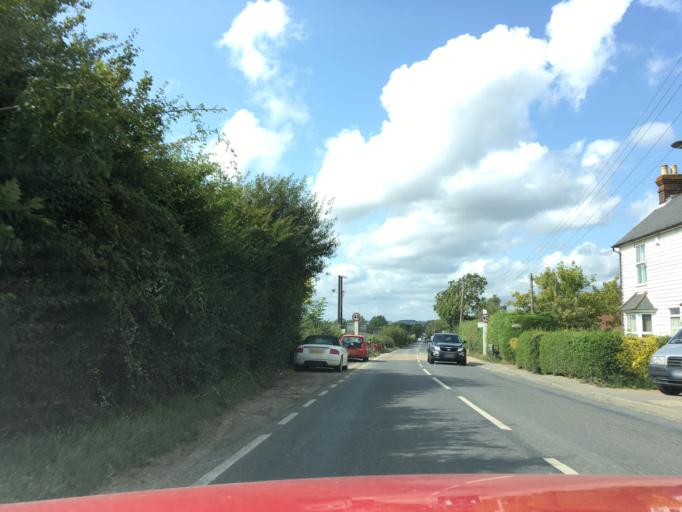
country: GB
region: England
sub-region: Kent
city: Headcorn
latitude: 51.1740
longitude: 0.6158
